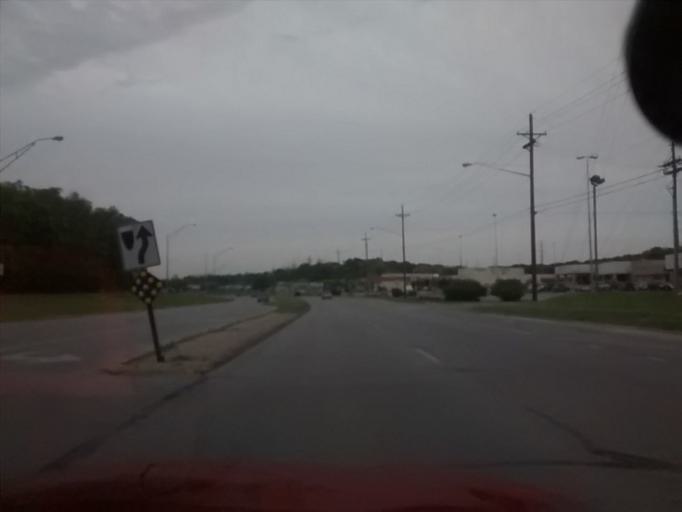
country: US
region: Nebraska
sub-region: Sarpy County
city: Bellevue
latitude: 41.1732
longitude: -95.9256
